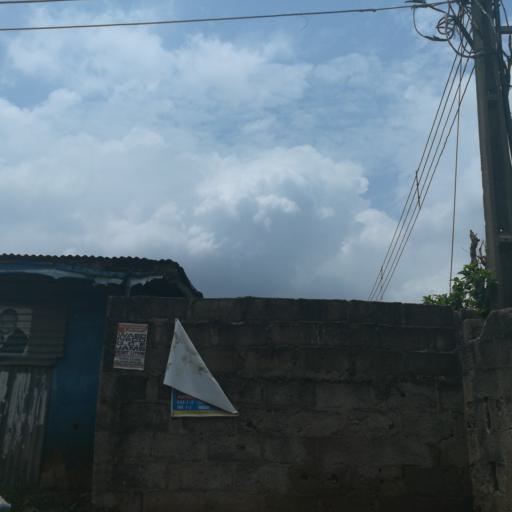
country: NG
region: Lagos
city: Ojota
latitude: 6.5812
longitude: 3.3815
